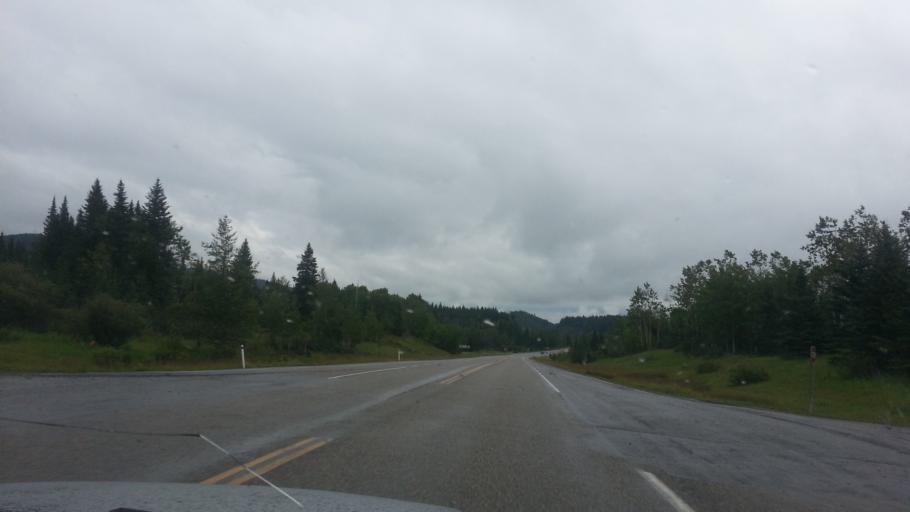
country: CA
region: Alberta
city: Cochrane
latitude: 50.8950
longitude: -114.7032
